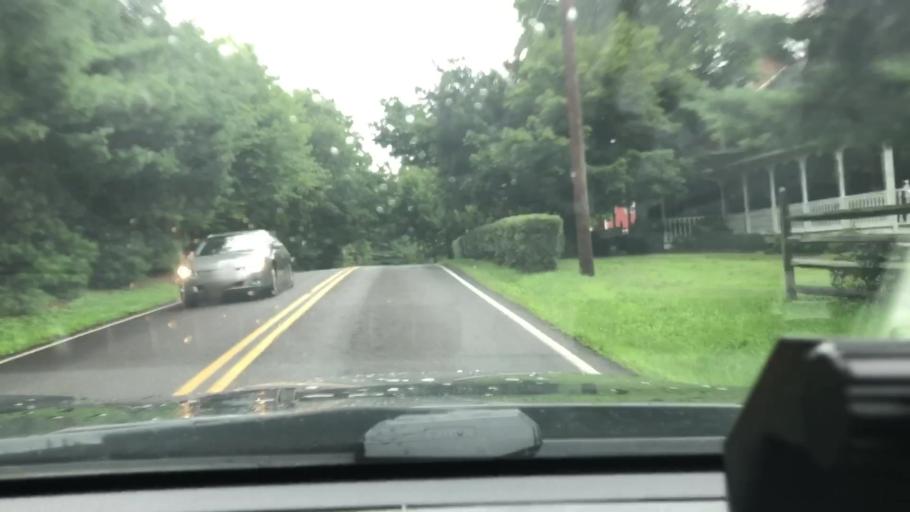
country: US
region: Pennsylvania
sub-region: Lehigh County
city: Coopersburg
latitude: 40.4887
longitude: -75.3952
